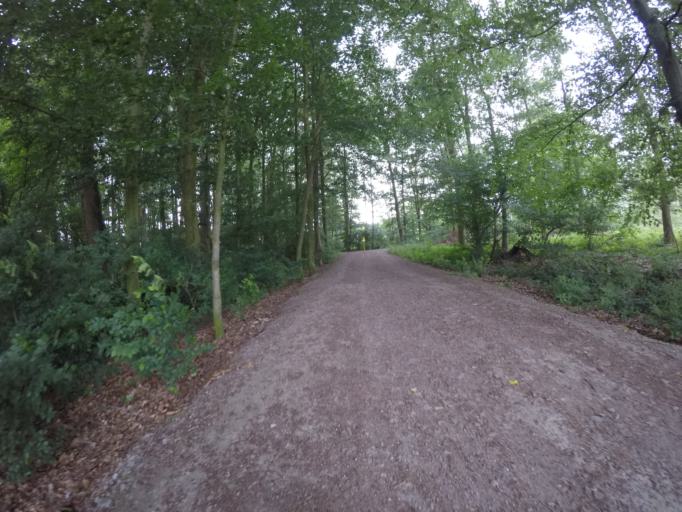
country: DE
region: North Rhine-Westphalia
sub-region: Regierungsbezirk Munster
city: Isselburg
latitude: 51.8553
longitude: 6.4239
